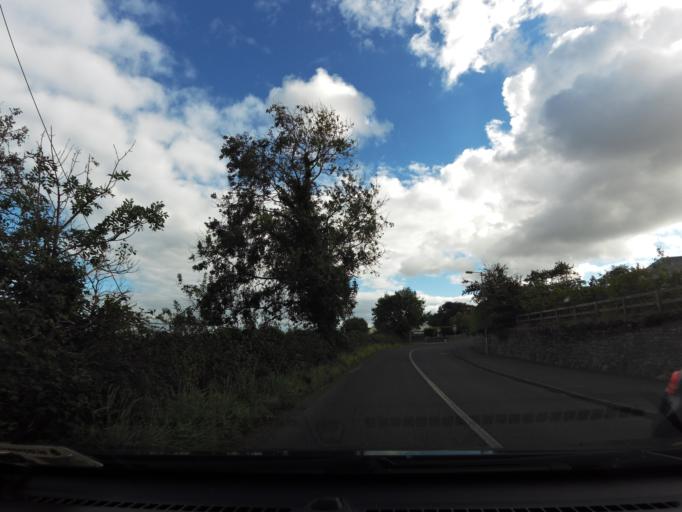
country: IE
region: Connaught
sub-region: County Galway
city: Moycullen
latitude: 53.3424
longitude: -9.1753
